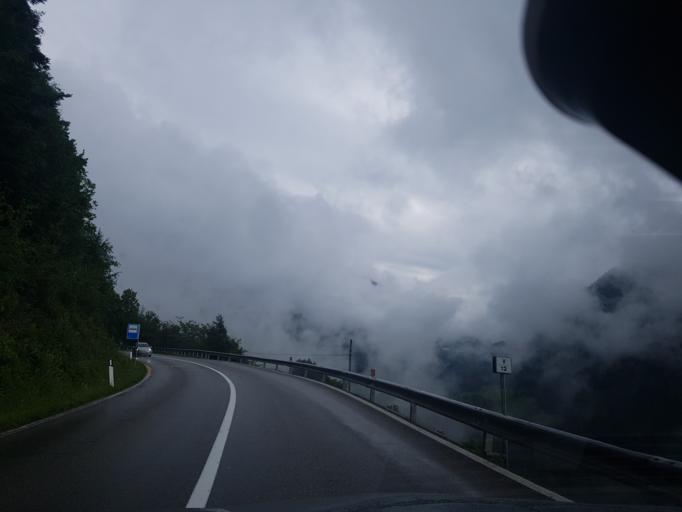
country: IT
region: Trentino-Alto Adige
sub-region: Bolzano
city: Laion
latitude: 46.5986
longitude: 11.6077
